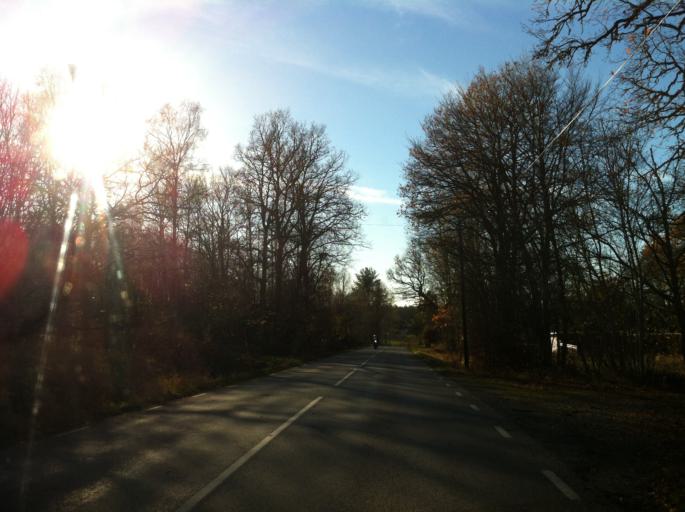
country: SE
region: Blekinge
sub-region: Ronneby Kommun
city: Brakne-Hoby
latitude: 56.2142
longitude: 15.0977
